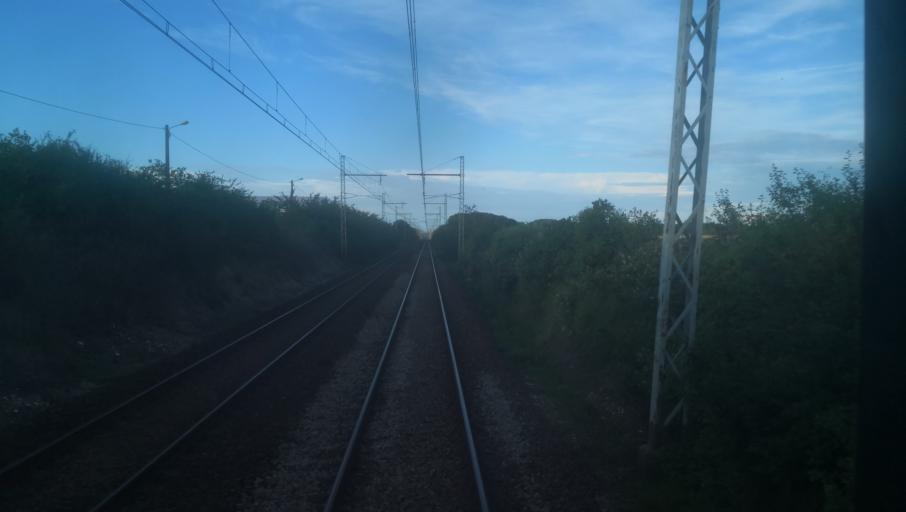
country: FR
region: Centre
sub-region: Departement de l'Indre
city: Neuvy-Pailloux
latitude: 46.8734
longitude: 1.8466
